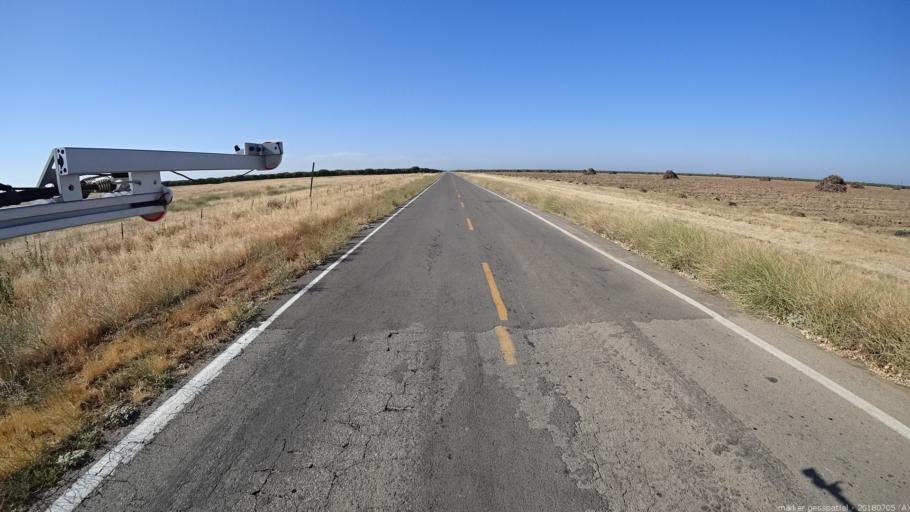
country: US
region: California
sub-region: Madera County
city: Madera Acres
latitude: 37.1147
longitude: -120.0746
